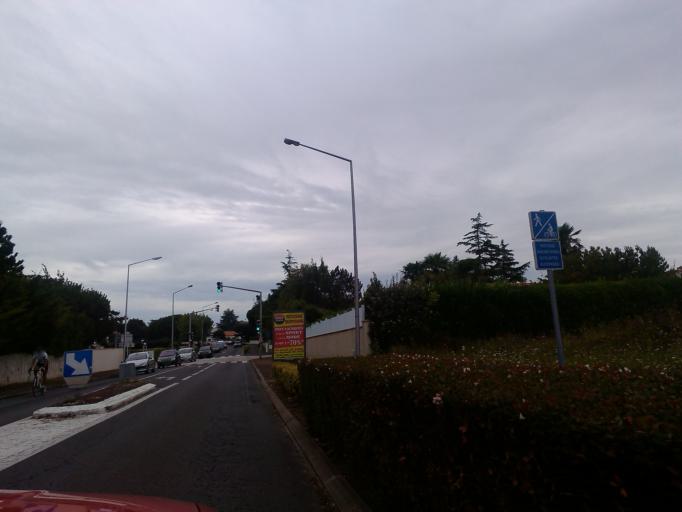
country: FR
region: Poitou-Charentes
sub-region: Departement de la Charente-Maritime
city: Vaux-sur-Mer
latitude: 45.6470
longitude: -1.0574
